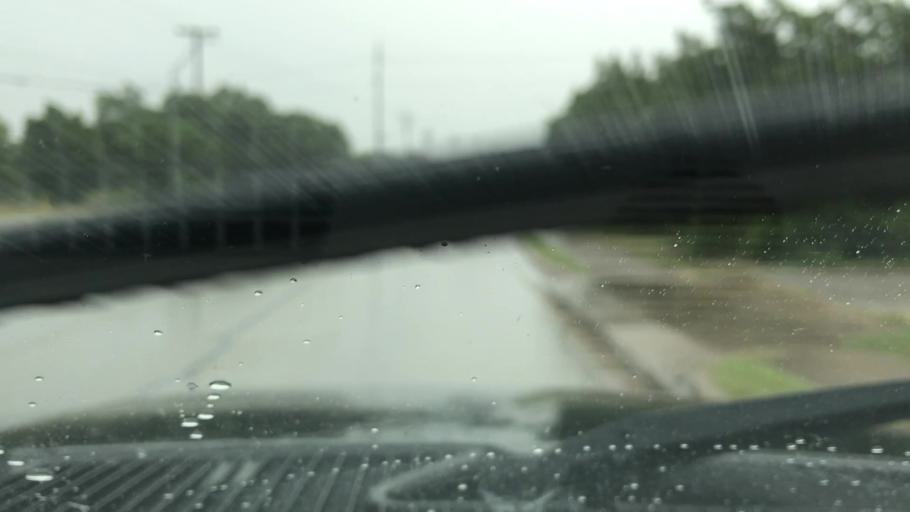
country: US
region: Texas
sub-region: Williamson County
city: Cedar Park
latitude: 30.4940
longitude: -97.8267
